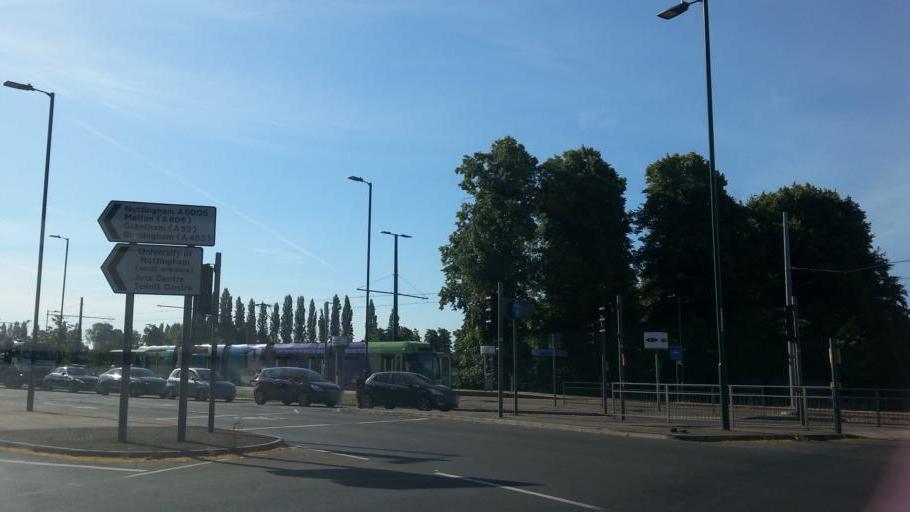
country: GB
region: England
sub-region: Nottingham
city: Nottingham
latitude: 52.9326
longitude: -1.2029
